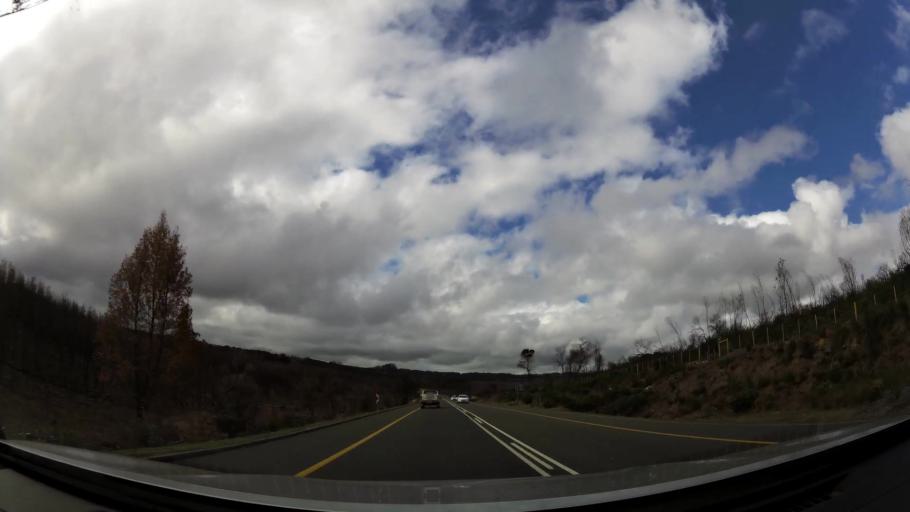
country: ZA
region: Western Cape
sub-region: Eden District Municipality
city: Knysna
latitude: -34.0368
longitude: 23.1496
